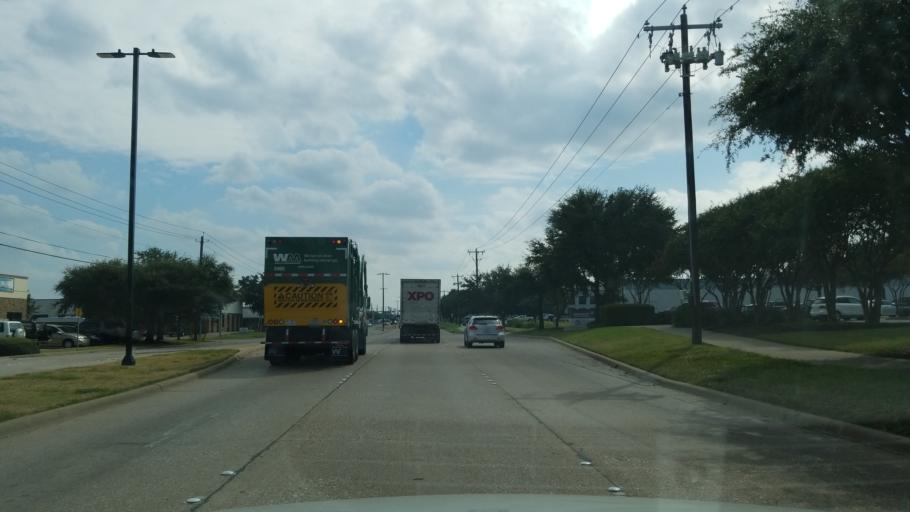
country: US
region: Texas
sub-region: Dallas County
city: Garland
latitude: 32.8923
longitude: -96.6831
